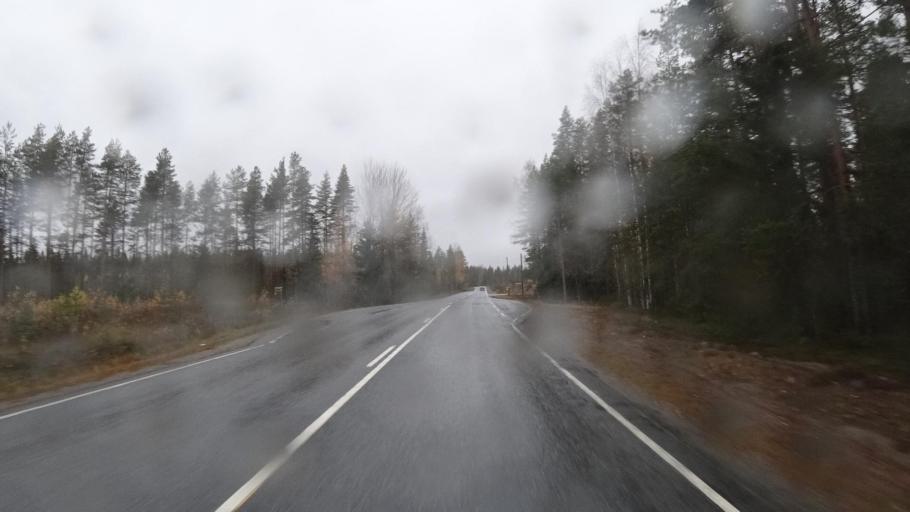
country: FI
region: Northern Savo
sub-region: Koillis-Savo
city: Tuusniemi
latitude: 62.8675
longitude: 28.4221
